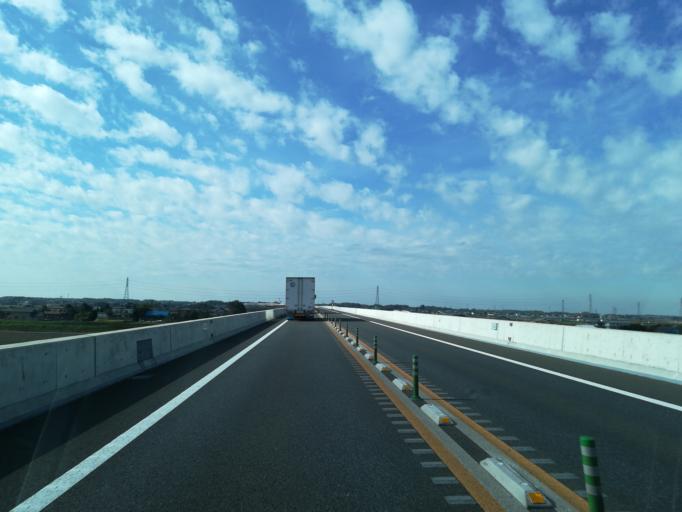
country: JP
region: Ibaraki
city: Ishige
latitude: 36.0795
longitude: 139.9942
